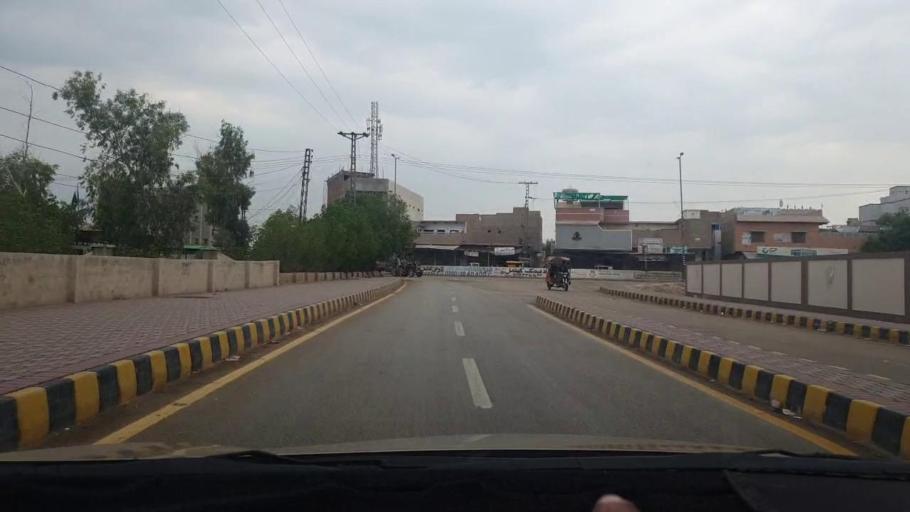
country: PK
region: Sindh
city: Larkana
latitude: 27.5660
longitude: 68.1981
